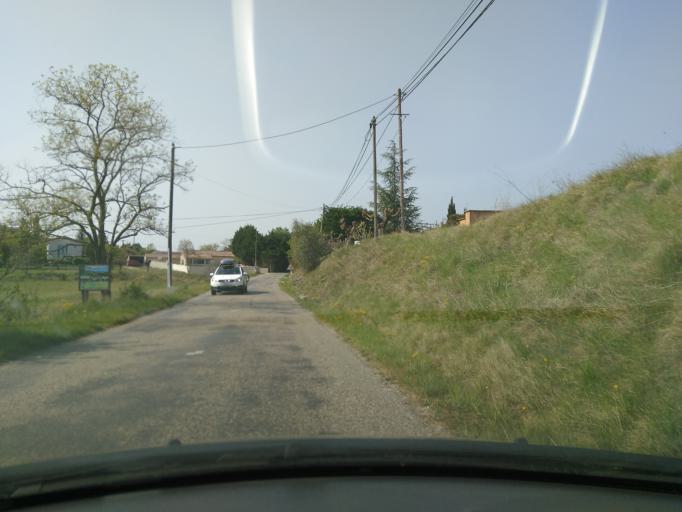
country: FR
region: Rhone-Alpes
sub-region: Departement de l'Ardeche
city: Ruoms
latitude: 44.4541
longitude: 4.3989
